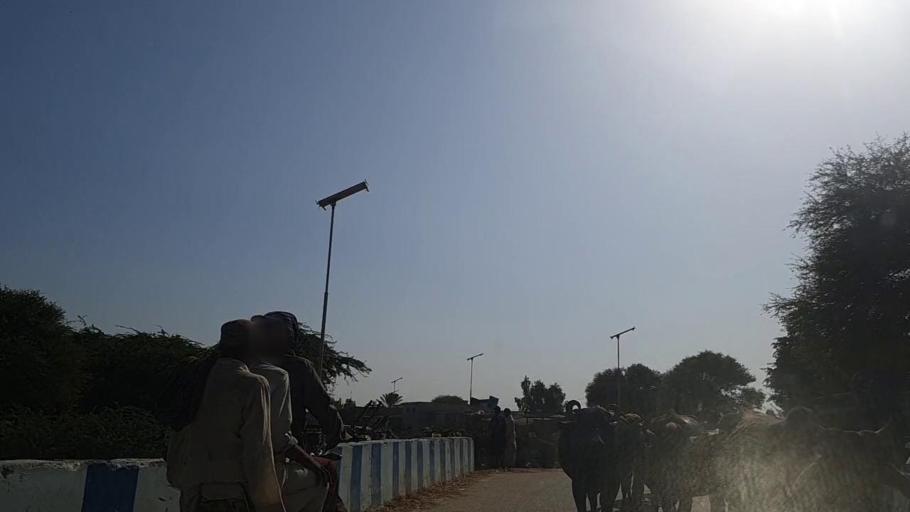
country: PK
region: Sindh
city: Jati
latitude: 24.4242
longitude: 68.2575
